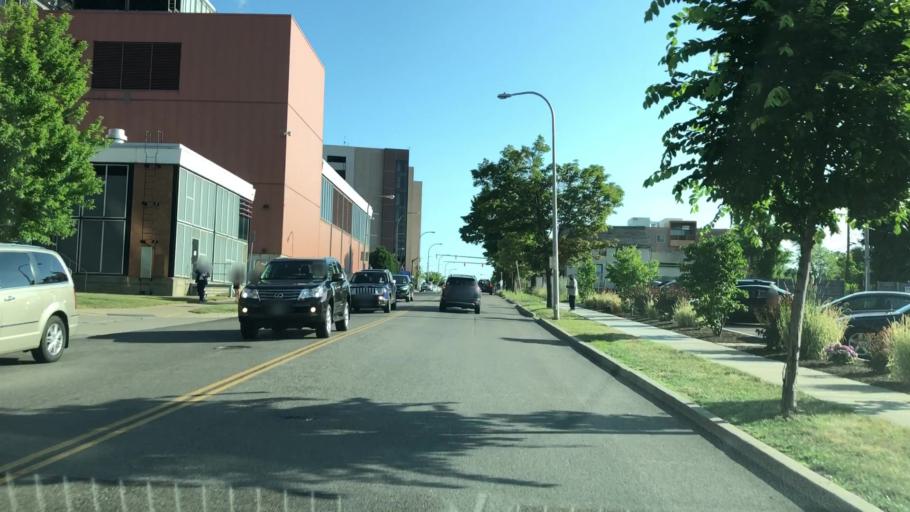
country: US
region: New York
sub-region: Erie County
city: Buffalo
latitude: 42.8990
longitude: -78.8634
